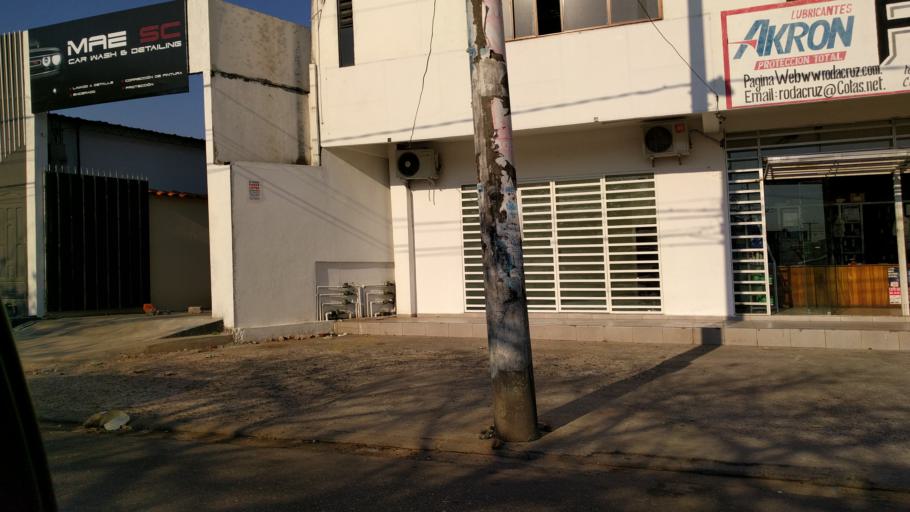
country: BO
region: Santa Cruz
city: Santa Cruz de la Sierra
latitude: -17.7723
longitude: -63.1674
